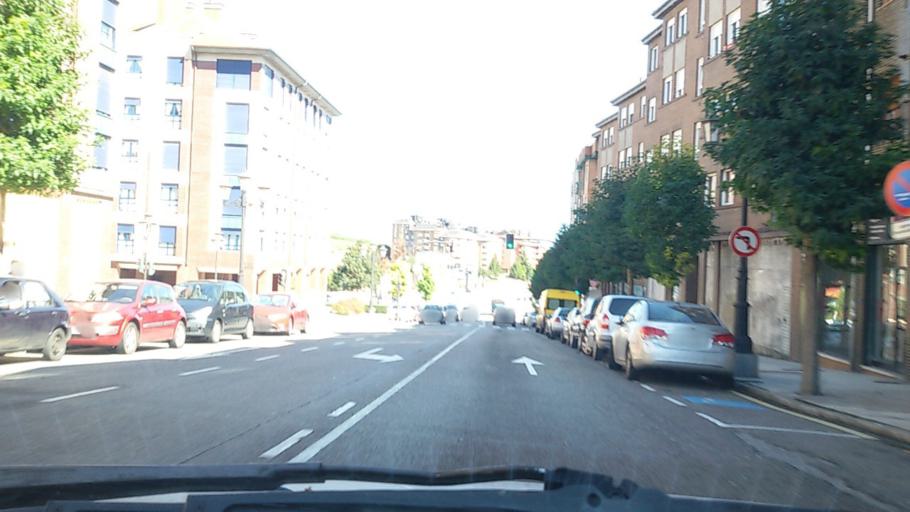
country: ES
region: Asturias
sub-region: Province of Asturias
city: Oviedo
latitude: 43.3758
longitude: -5.8348
